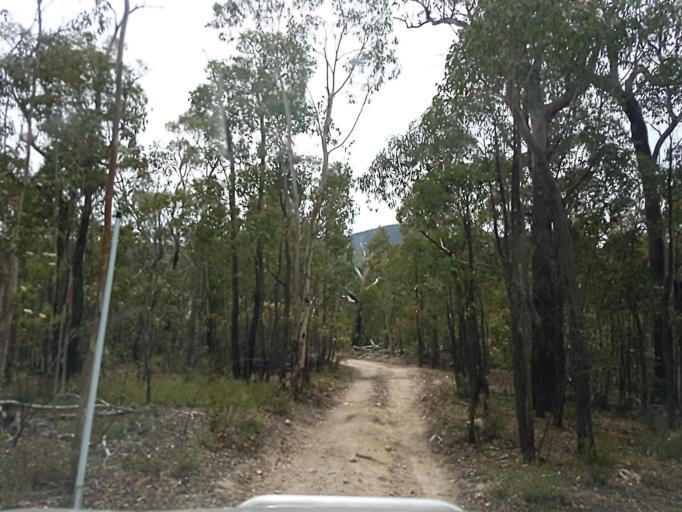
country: AU
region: New South Wales
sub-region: Snowy River
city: Jindabyne
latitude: -36.8375
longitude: 148.2365
